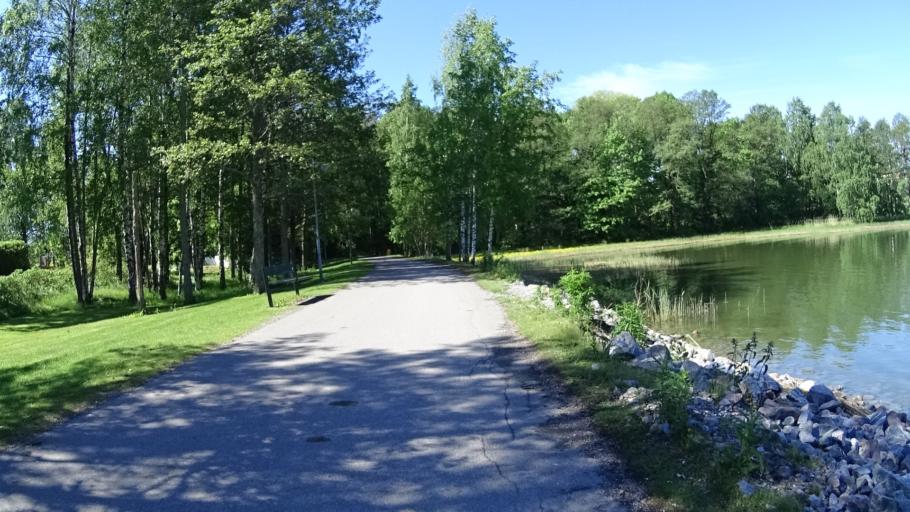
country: FI
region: Uusimaa
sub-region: Helsinki
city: Teekkarikylae
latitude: 60.1701
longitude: 24.8608
